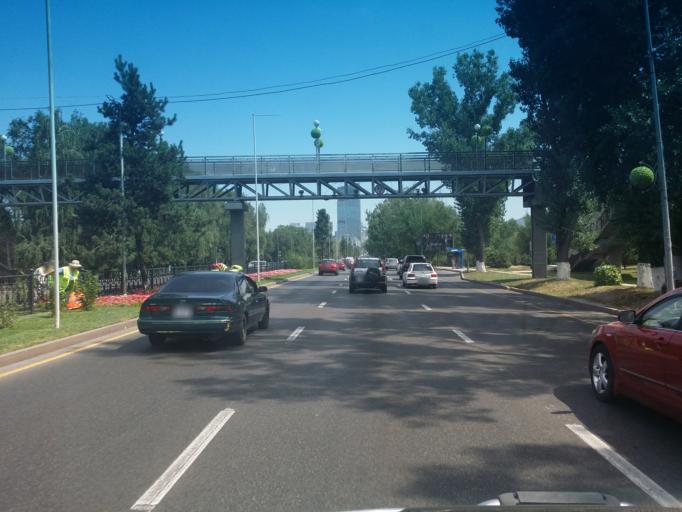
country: KZ
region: Almaty Qalasy
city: Almaty
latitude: 43.2096
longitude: 76.9166
